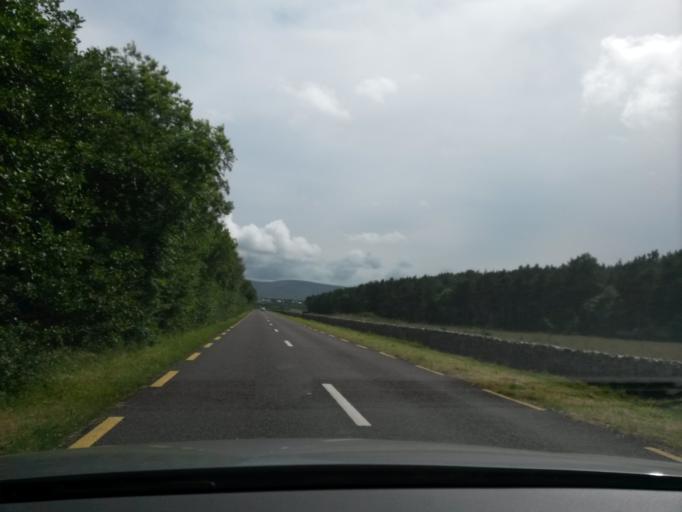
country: IE
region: Connaught
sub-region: County Leitrim
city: Kinlough
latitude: 54.4477
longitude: -8.4544
